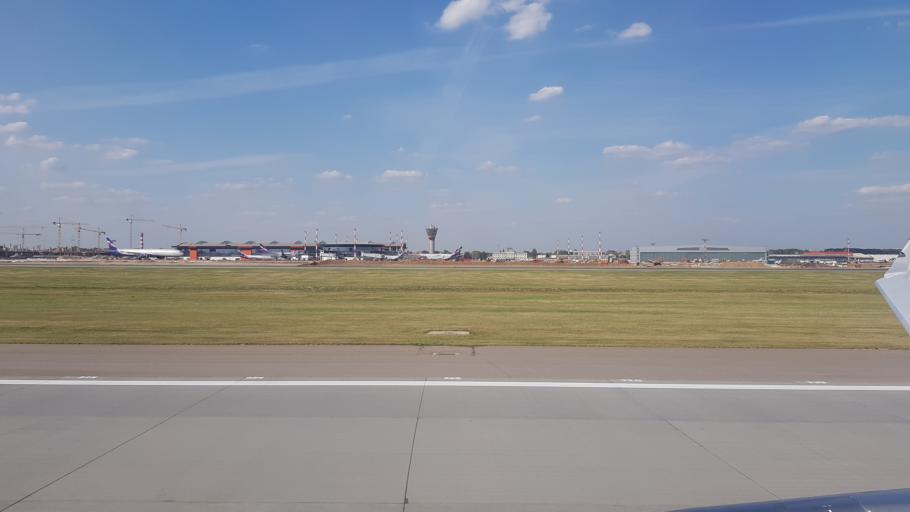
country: RU
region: Moskovskaya
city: Lobnya
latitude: 55.9726
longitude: 37.4229
